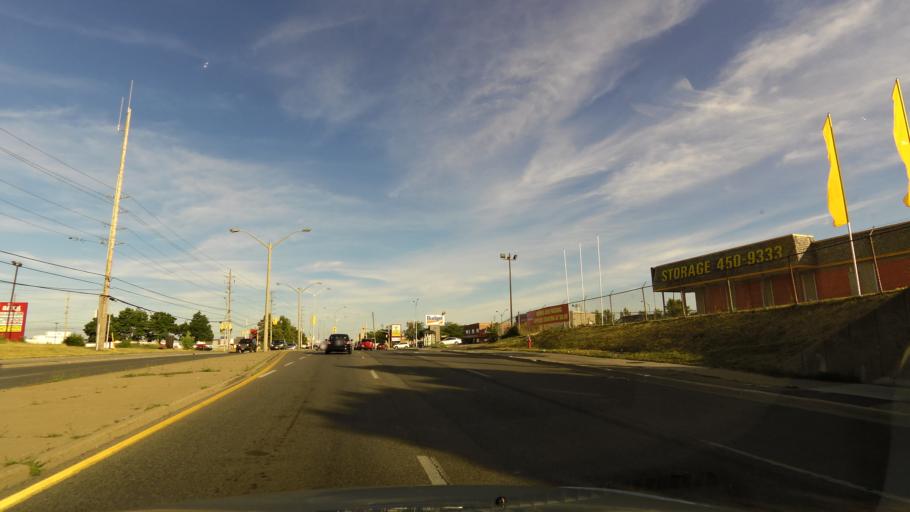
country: CA
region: Ontario
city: Brampton
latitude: 43.6905
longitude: -79.7426
